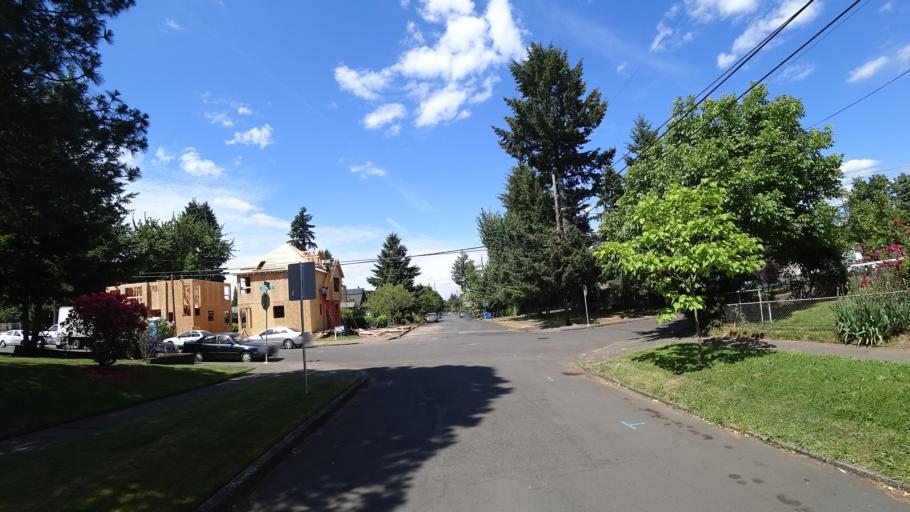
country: US
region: Oregon
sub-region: Multnomah County
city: Portland
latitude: 45.5822
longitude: -122.7124
